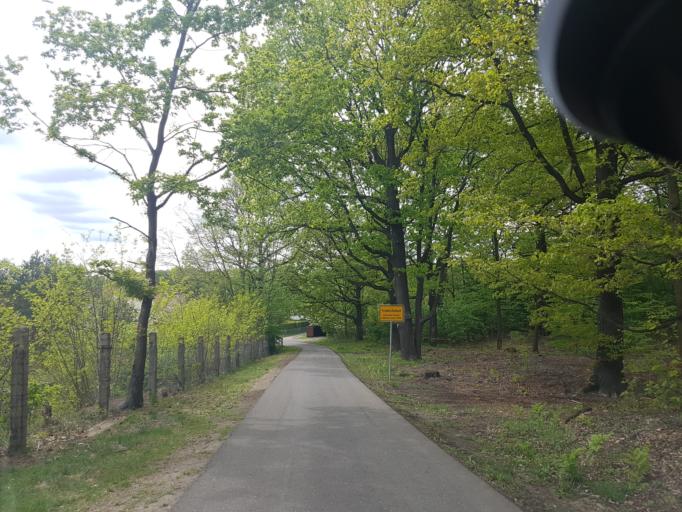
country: DE
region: Saxony
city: Gross Duben
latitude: 51.6067
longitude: 14.5735
